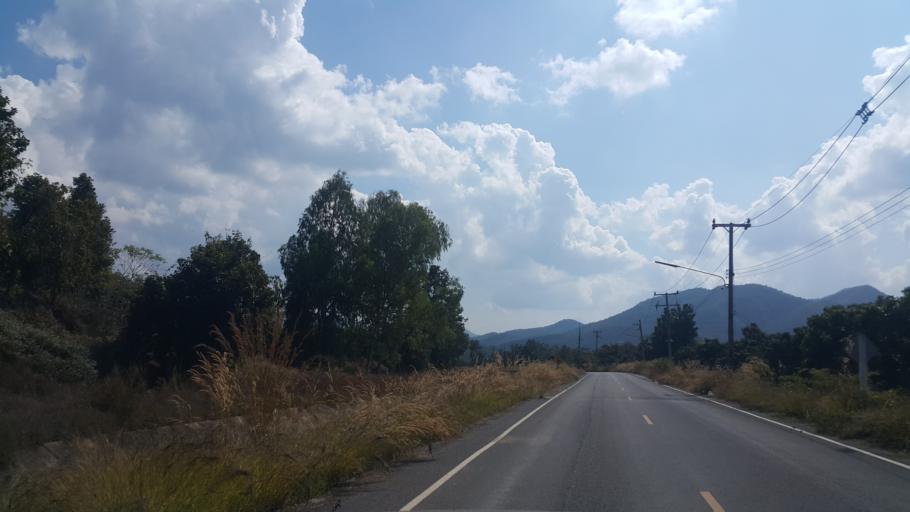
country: TH
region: Lamphun
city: Ban Thi
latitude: 18.6310
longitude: 99.1595
